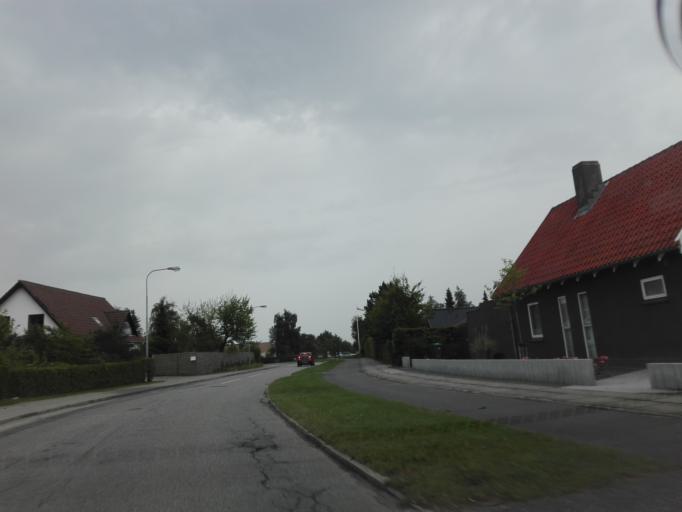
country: DK
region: Central Jutland
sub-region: Arhus Kommune
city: Hjortshoj
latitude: 56.2025
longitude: 10.2697
